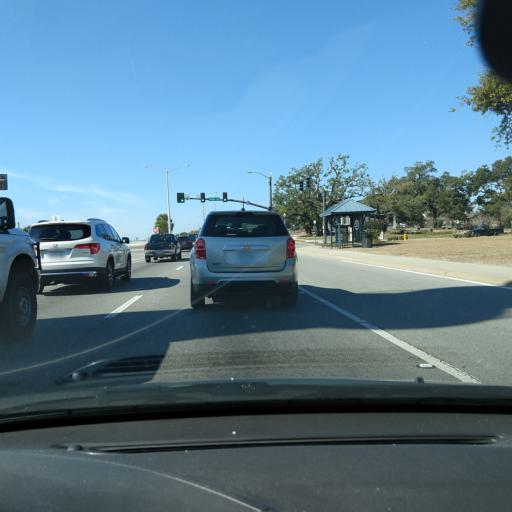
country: US
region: Mississippi
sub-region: Harrison County
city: Biloxi
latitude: 30.3946
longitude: -88.9012
